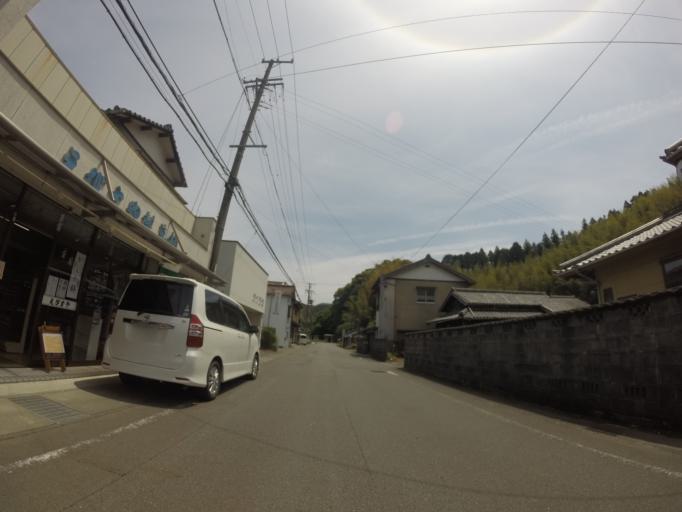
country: JP
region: Shizuoka
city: Fujieda
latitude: 34.9184
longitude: 138.2402
